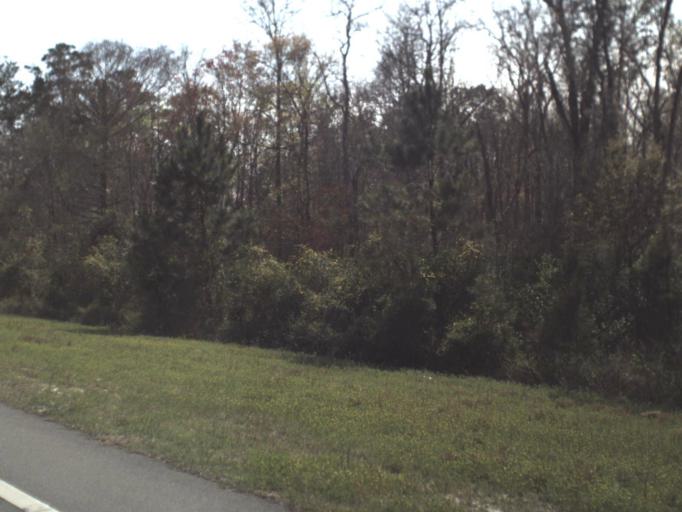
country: US
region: Florida
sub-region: Franklin County
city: Carrabelle
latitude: 29.9915
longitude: -84.5030
